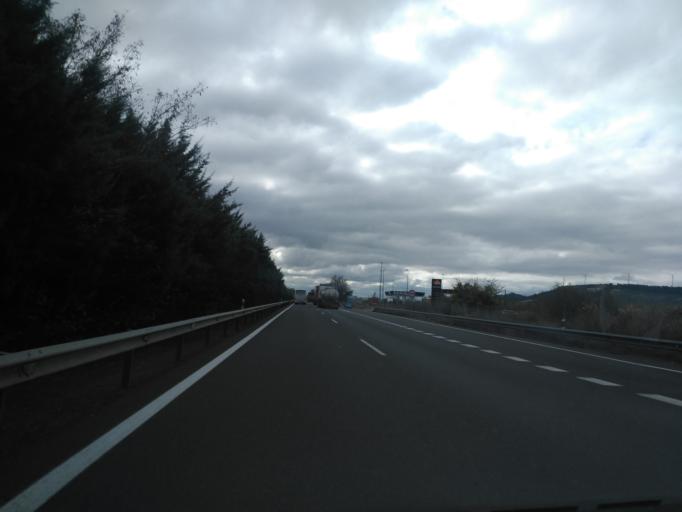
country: ES
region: Castille and Leon
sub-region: Provincia de Palencia
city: Venta de Banos
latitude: 41.9149
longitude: -4.5105
